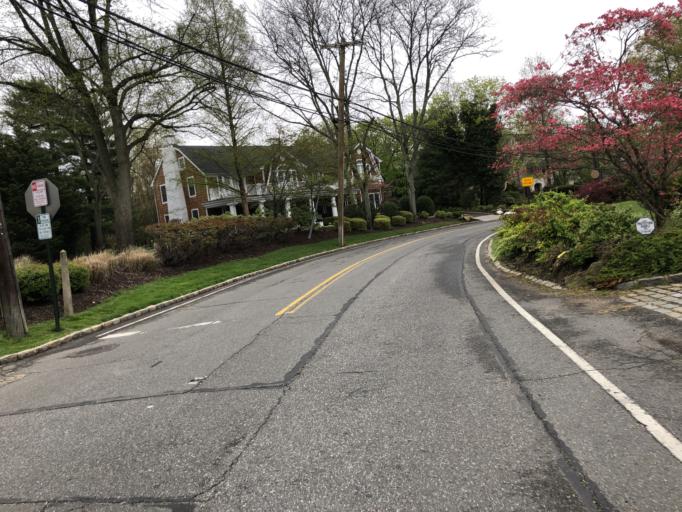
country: US
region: New York
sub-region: Nassau County
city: Woodmere
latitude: 40.6249
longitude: -73.7030
